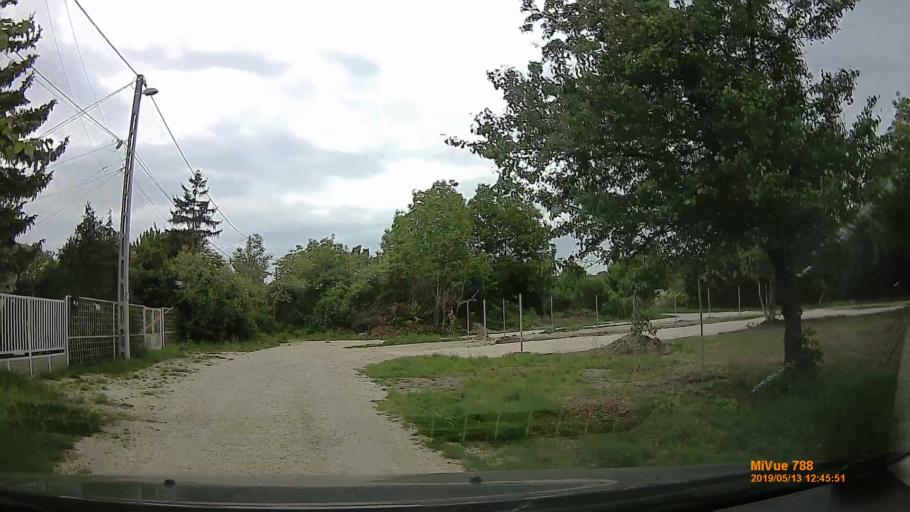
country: HU
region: Pest
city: Diosd
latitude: 47.4035
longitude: 18.9868
